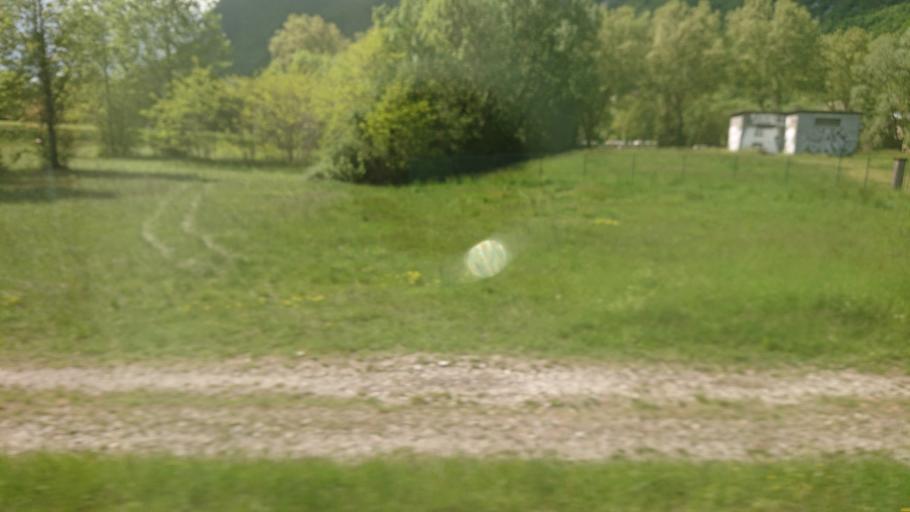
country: FR
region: Rhone-Alpes
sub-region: Departement de l'Ain
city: Culoz
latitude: 45.8515
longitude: 5.7963
